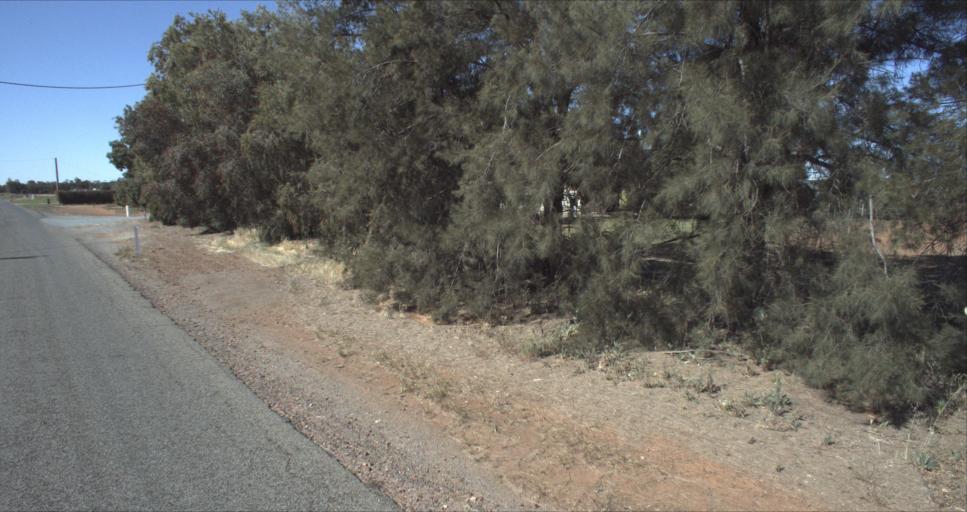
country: AU
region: New South Wales
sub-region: Leeton
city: Leeton
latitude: -34.5654
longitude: 146.3827
